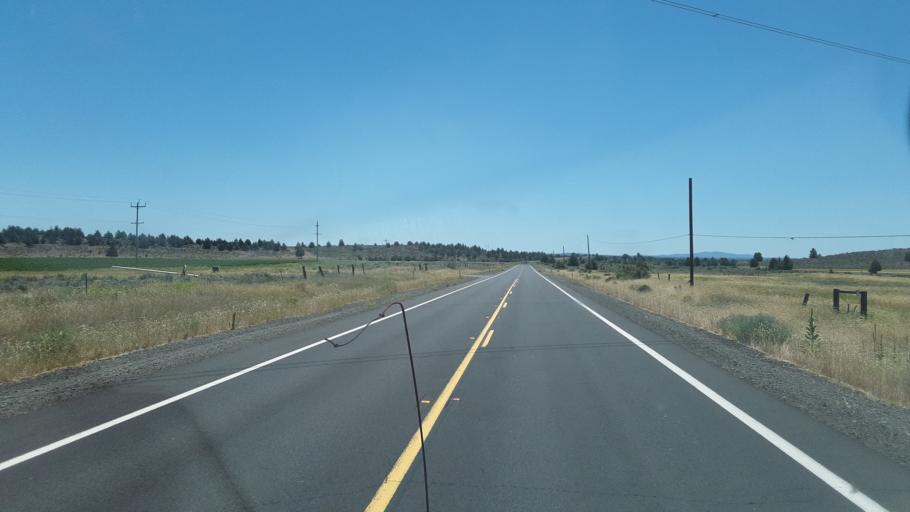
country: US
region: California
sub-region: Siskiyou County
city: Tulelake
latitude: 41.7186
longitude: -121.2914
